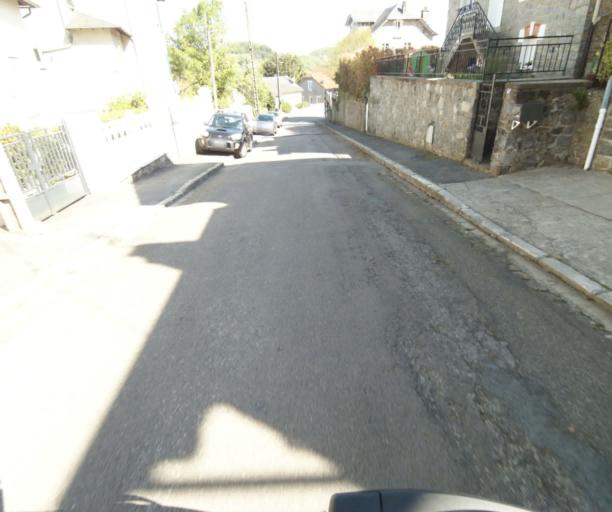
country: FR
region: Limousin
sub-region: Departement de la Correze
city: Tulle
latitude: 45.2701
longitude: 1.7782
